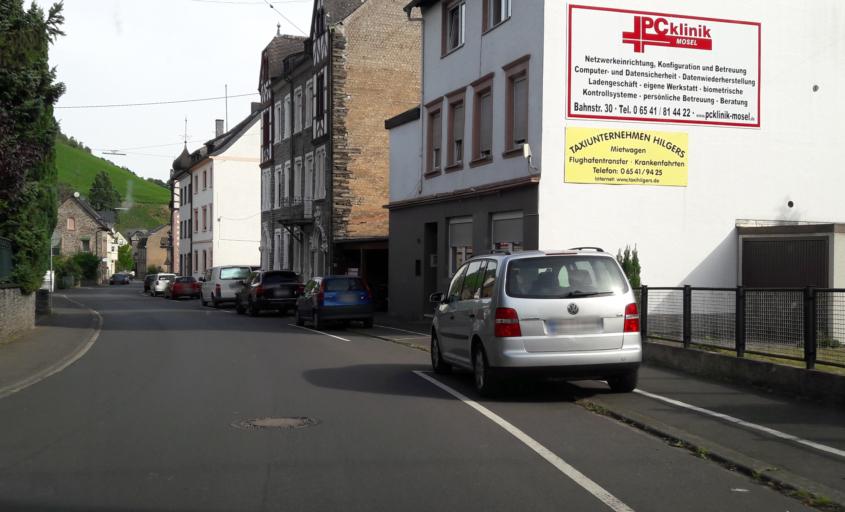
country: DE
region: Rheinland-Pfalz
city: Traben-Trarbach
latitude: 49.9416
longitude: 7.1098
